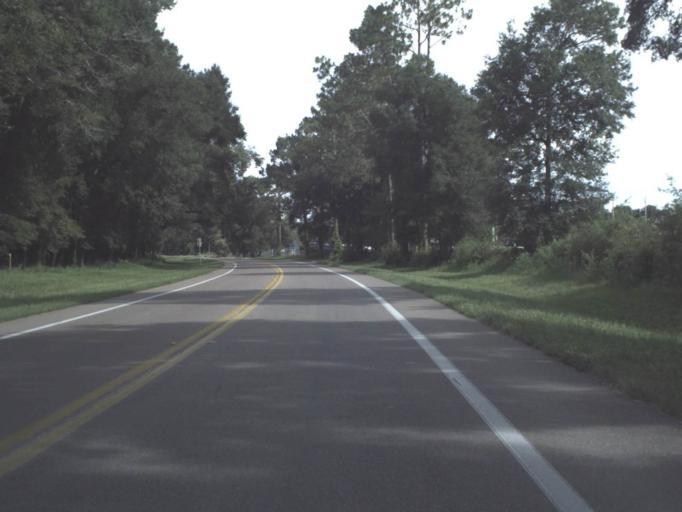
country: US
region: Florida
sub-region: Gilchrist County
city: Trenton
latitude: 29.6757
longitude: -82.8568
